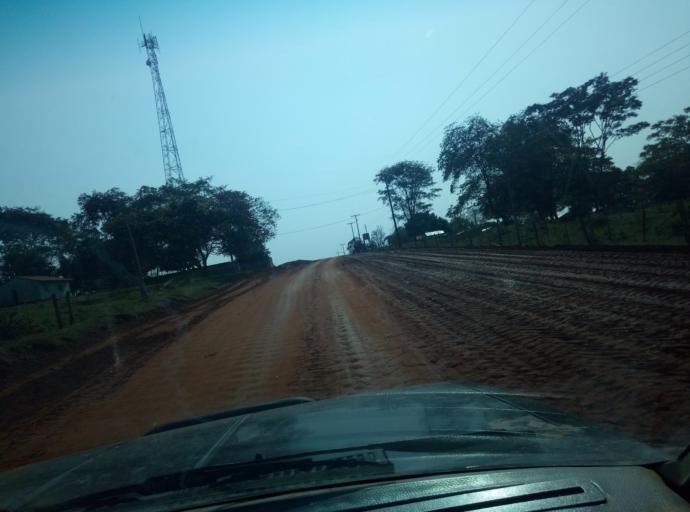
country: PY
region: Caaguazu
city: Carayao
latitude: -25.3159
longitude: -56.3275
